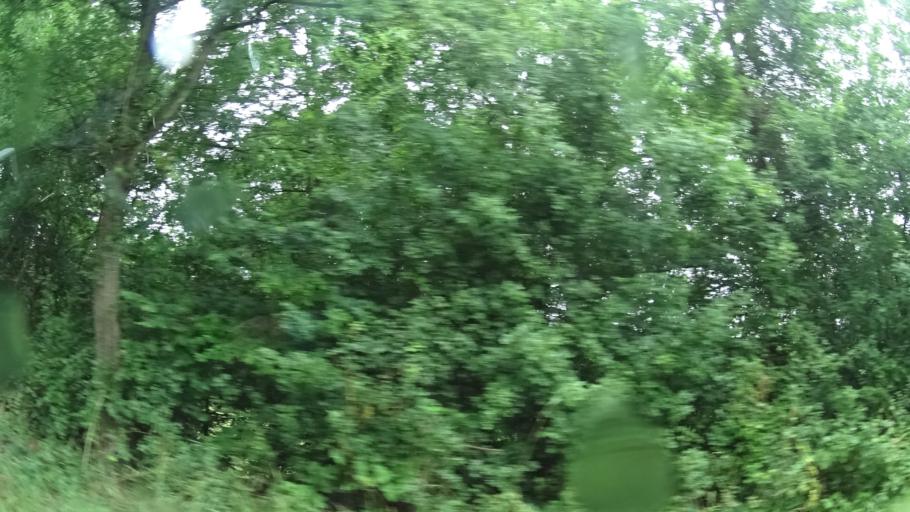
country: LU
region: Grevenmacher
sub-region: Canton de Remich
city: Mondorf-les-Bains
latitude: 49.5200
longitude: 6.2857
